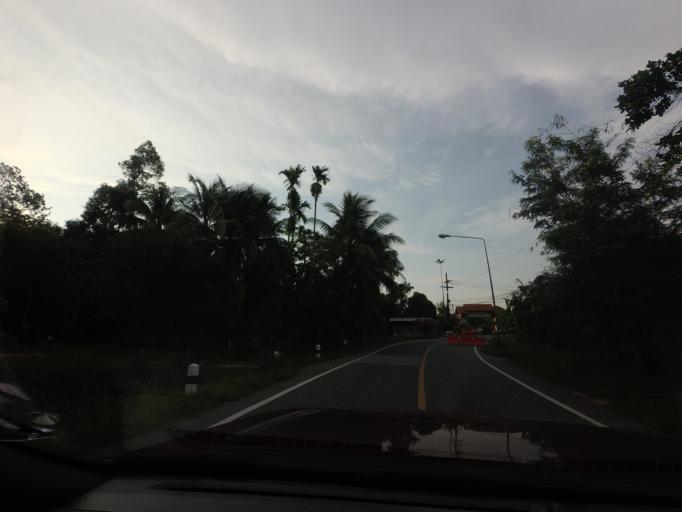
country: TH
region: Pattani
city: Khok Pho
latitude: 6.6694
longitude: 101.1010
